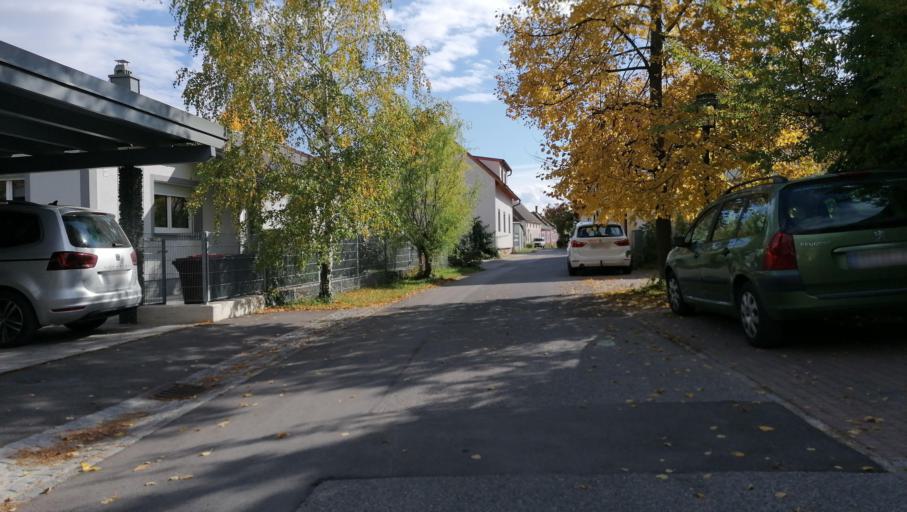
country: AT
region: Lower Austria
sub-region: Politischer Bezirk Baden
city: Tattendorf
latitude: 47.9596
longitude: 16.2996
